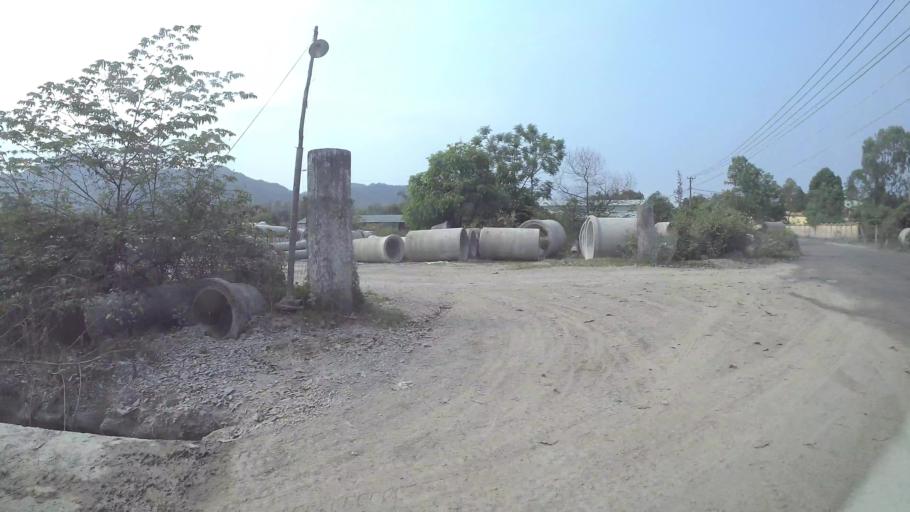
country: VN
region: Da Nang
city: Lien Chieu
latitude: 16.0453
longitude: 108.1512
